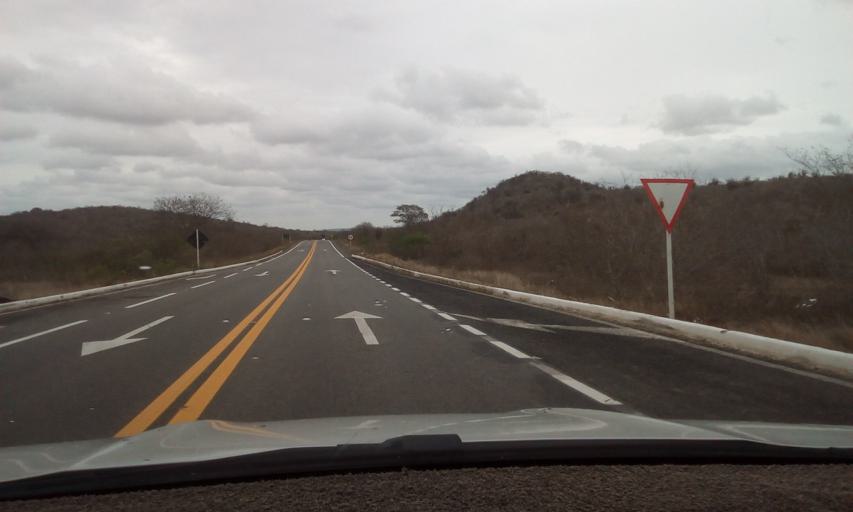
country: BR
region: Paraiba
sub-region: Areia
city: Remigio
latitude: -6.8887
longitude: -35.9159
